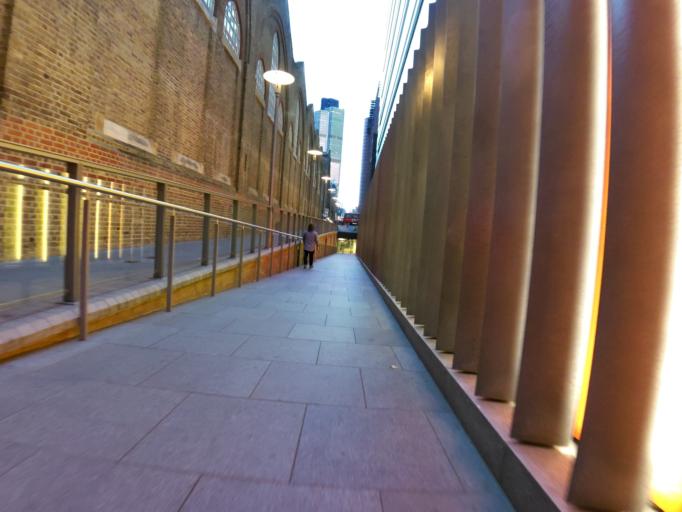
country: GB
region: England
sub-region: Greater London
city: City of London
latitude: 51.5194
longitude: -0.0820
